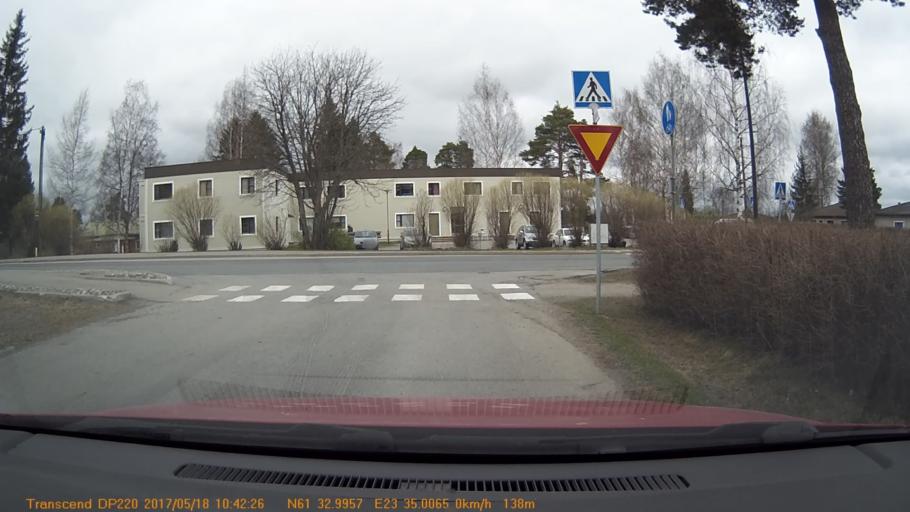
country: FI
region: Pirkanmaa
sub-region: Tampere
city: Yloejaervi
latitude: 61.5499
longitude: 23.5835
